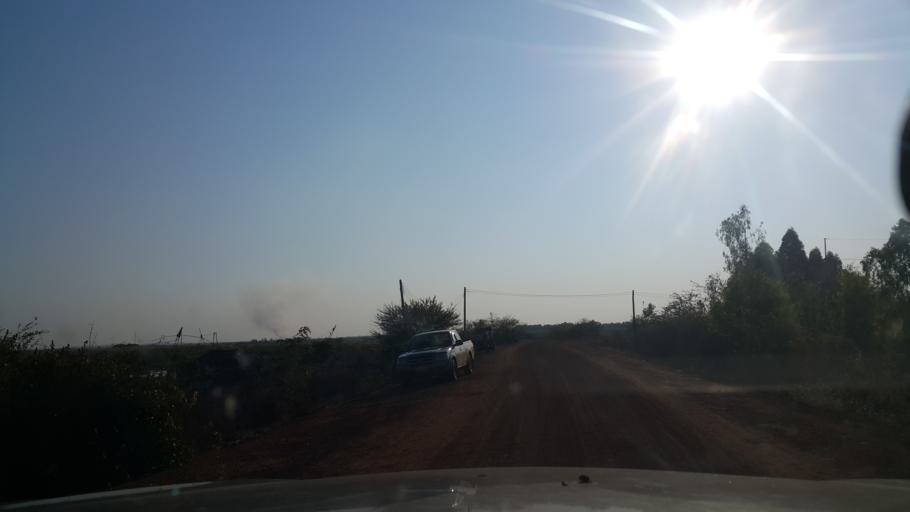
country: TH
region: Changwat Udon Thani
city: Ban Na Muang
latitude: 17.2236
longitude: 103.0467
